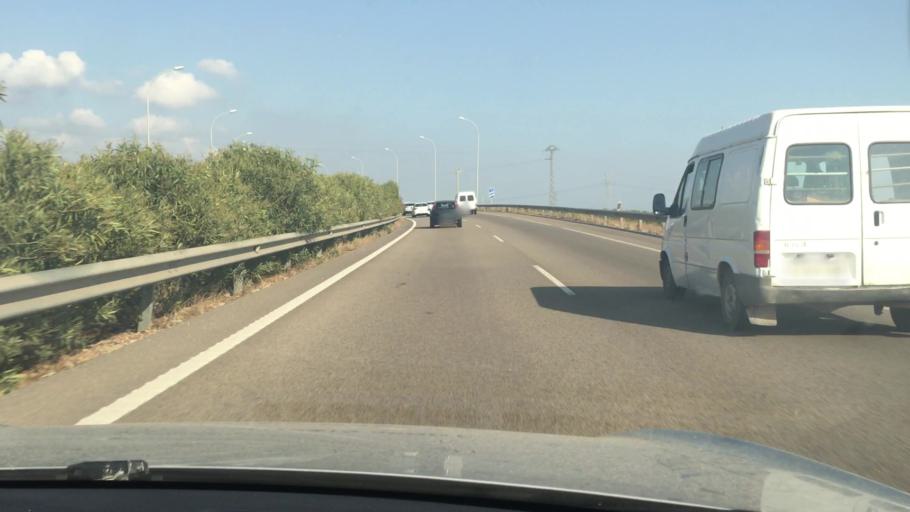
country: ES
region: Valencia
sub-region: Provincia de Castello
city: Vila-real
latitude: 39.9848
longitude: -0.1272
